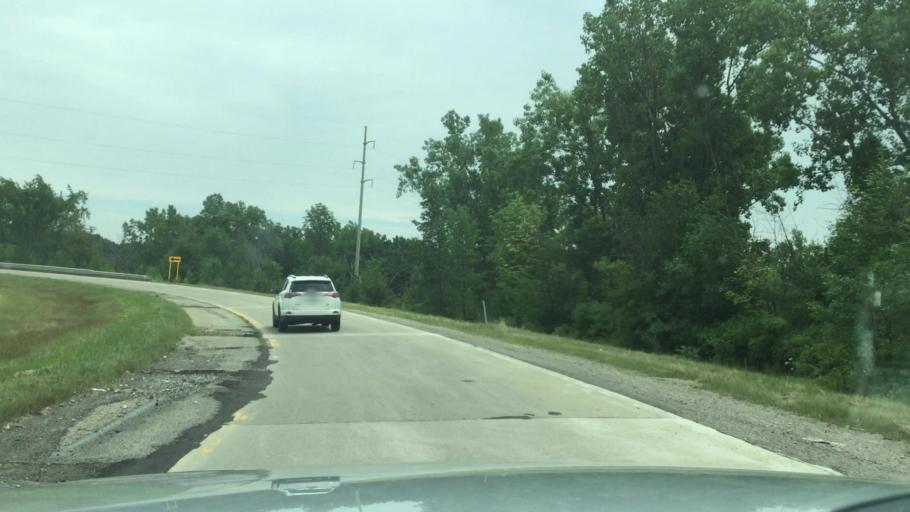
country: US
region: Michigan
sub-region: Genesee County
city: Swartz Creek
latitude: 42.9643
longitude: -83.8084
